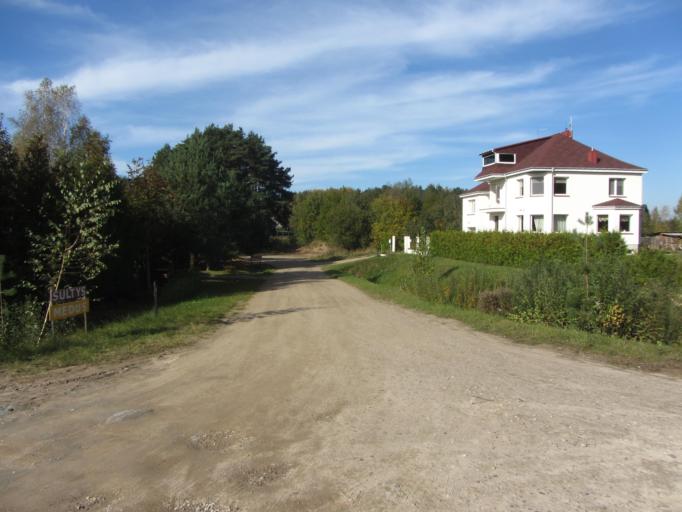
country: LT
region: Vilnius County
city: Elektrenai
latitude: 54.7840
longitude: 24.7087
